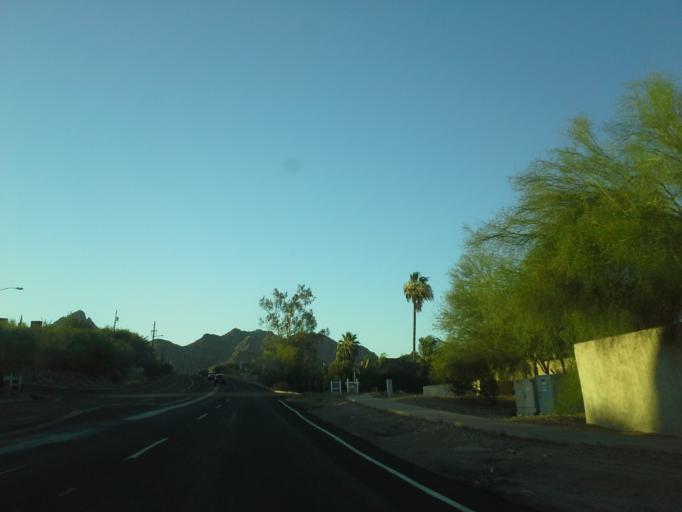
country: US
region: Arizona
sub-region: Maricopa County
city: Paradise Valley
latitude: 33.5189
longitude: -112.0129
